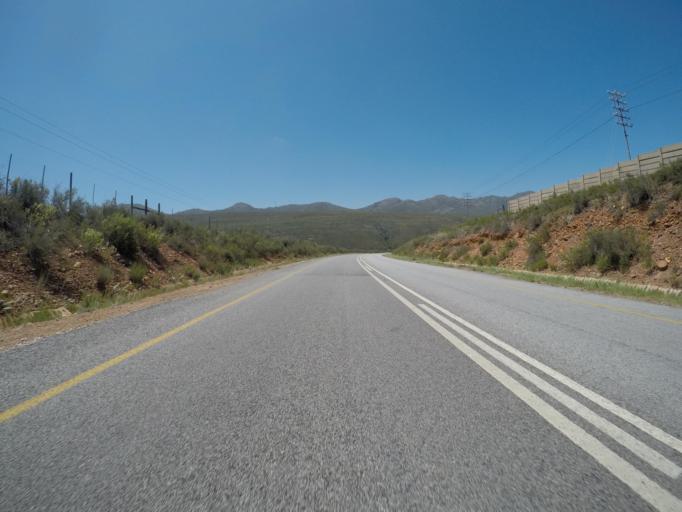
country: ZA
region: Eastern Cape
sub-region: Cacadu District Municipality
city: Kareedouw
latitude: -33.9447
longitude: 24.3052
